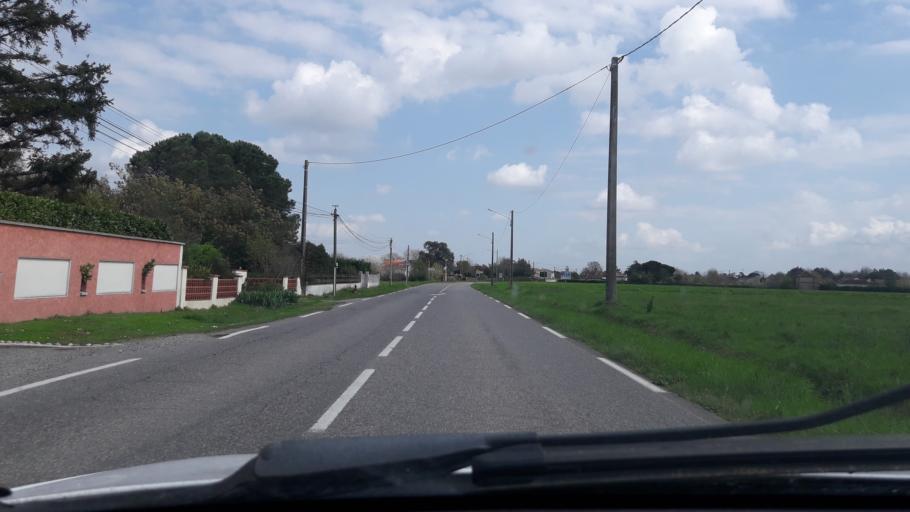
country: FR
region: Midi-Pyrenees
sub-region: Departement de la Haute-Garonne
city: Seysses
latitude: 43.4997
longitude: 1.2890
